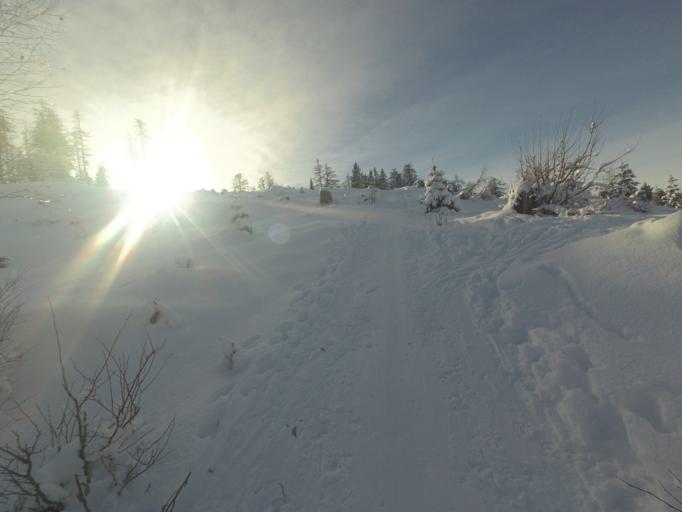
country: AT
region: Salzburg
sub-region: Politischer Bezirk Sankt Johann im Pongau
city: Sankt Johann im Pongau
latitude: 47.3139
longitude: 13.2232
